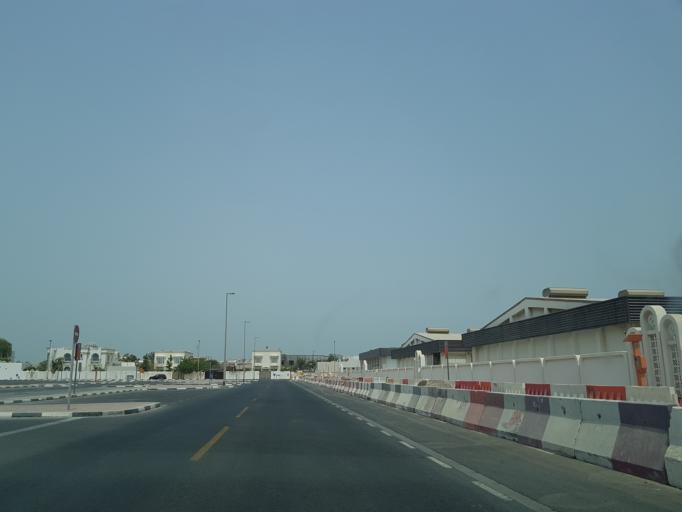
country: AE
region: Ash Shariqah
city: Sharjah
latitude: 25.2360
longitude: 55.2924
